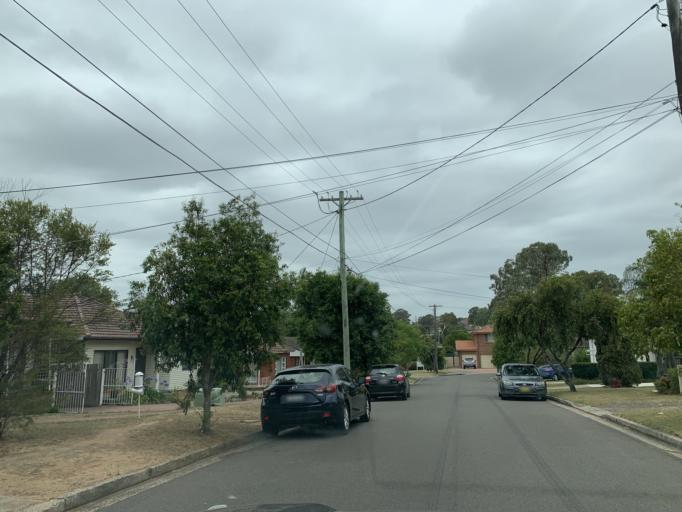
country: AU
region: New South Wales
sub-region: Blacktown
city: Blacktown
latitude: -33.7770
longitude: 150.8969
